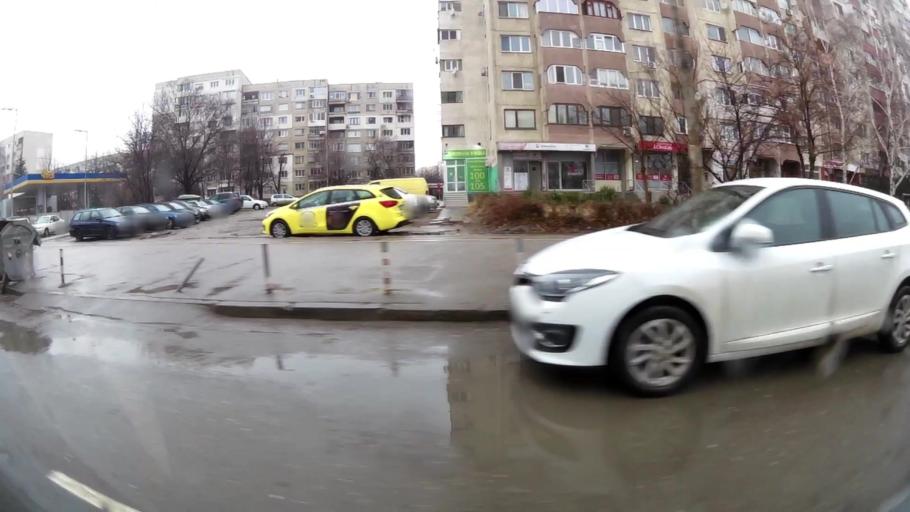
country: BG
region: Sofia-Capital
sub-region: Stolichna Obshtina
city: Sofia
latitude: 42.6395
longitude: 23.3815
